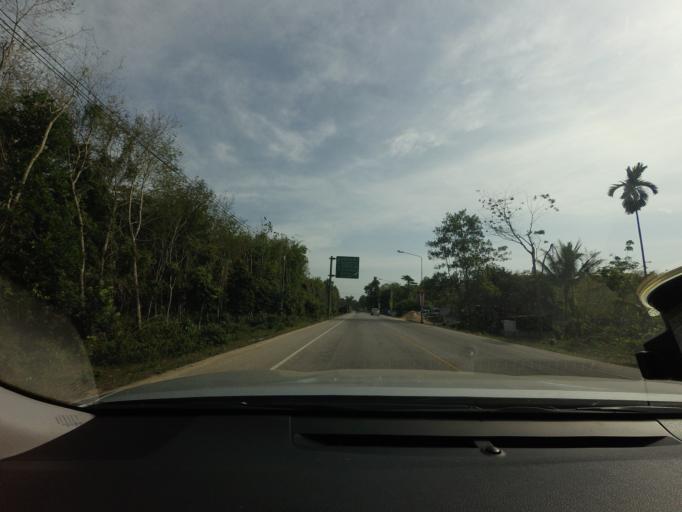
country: TH
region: Narathiwat
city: Ra-ngae
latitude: 6.3291
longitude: 101.7890
